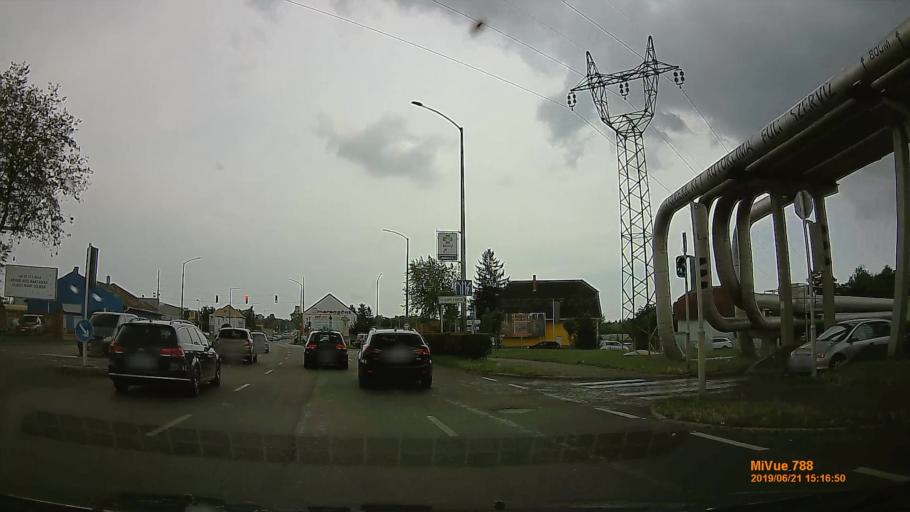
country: HU
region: Baranya
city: Pecs
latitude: 46.0610
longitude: 18.2302
